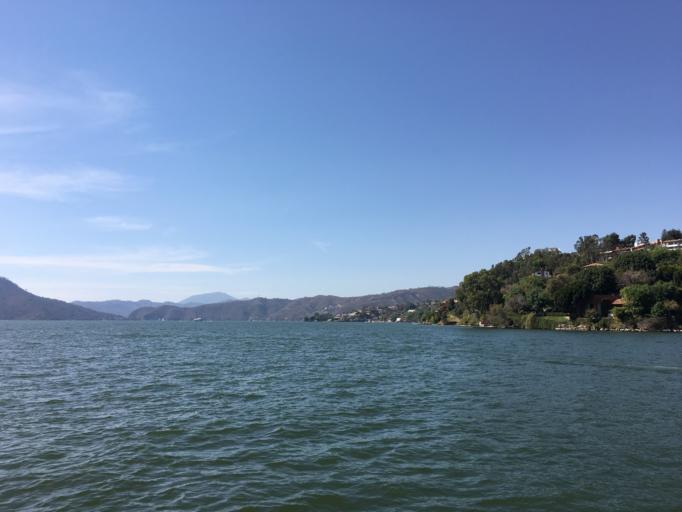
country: MX
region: Mexico
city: Valle de Bravo
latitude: 19.1889
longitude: -100.1348
